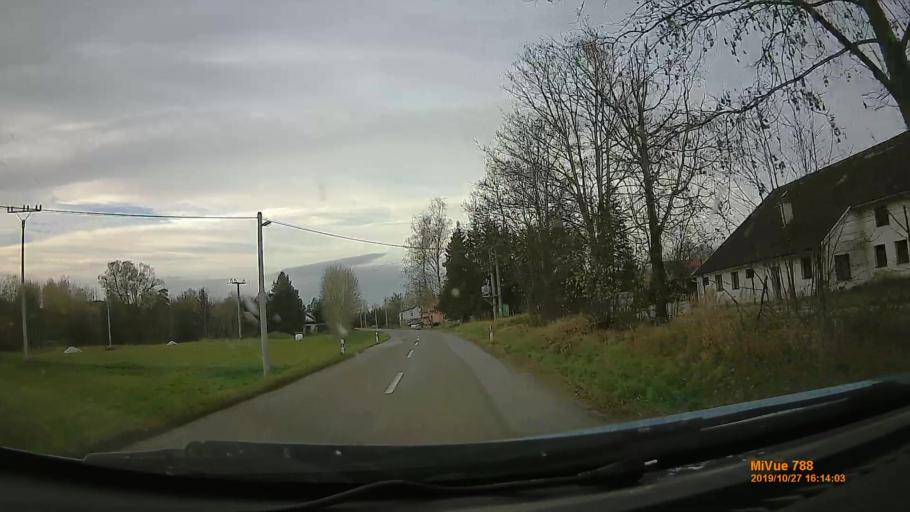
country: PL
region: Lower Silesian Voivodeship
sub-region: Powiat klodzki
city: Radkow
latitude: 50.5530
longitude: 16.3981
